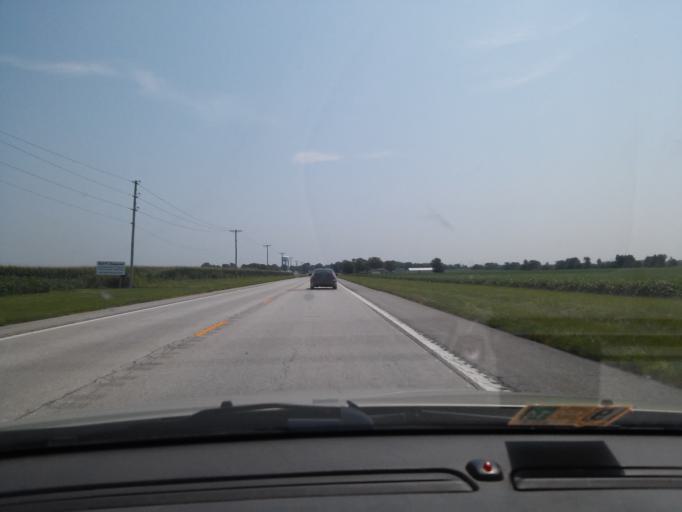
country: US
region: Missouri
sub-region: Audrain County
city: Vandalia
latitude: 39.3458
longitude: -91.3598
